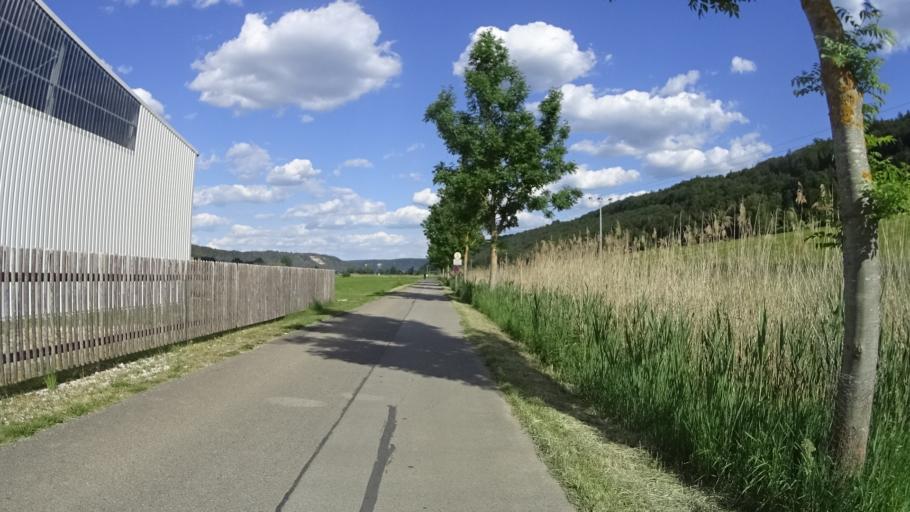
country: DE
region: Bavaria
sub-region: Upper Bavaria
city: Denkendorf
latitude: 49.0202
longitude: 11.4846
